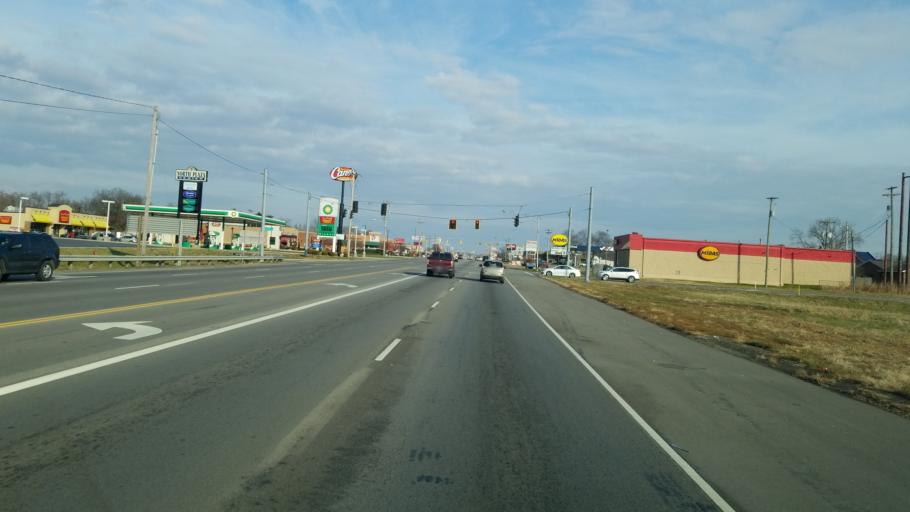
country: US
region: Ohio
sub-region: Ross County
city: Chillicothe
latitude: 39.3495
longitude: -82.9766
